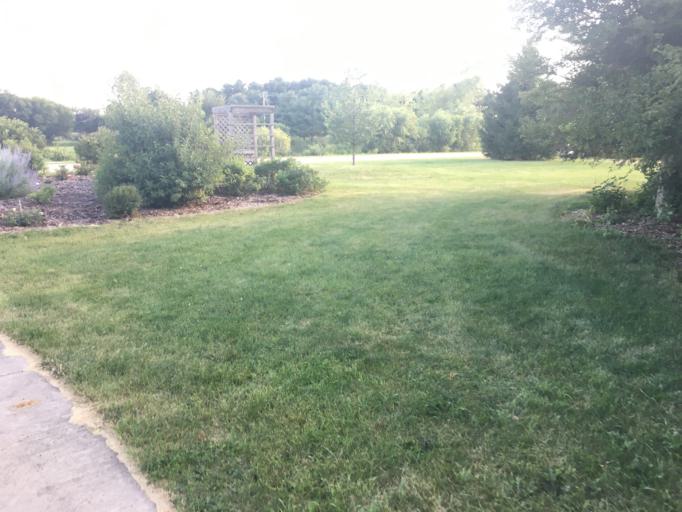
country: US
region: Minnesota
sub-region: Olmsted County
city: Rochester
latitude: 44.0197
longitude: -92.4378
